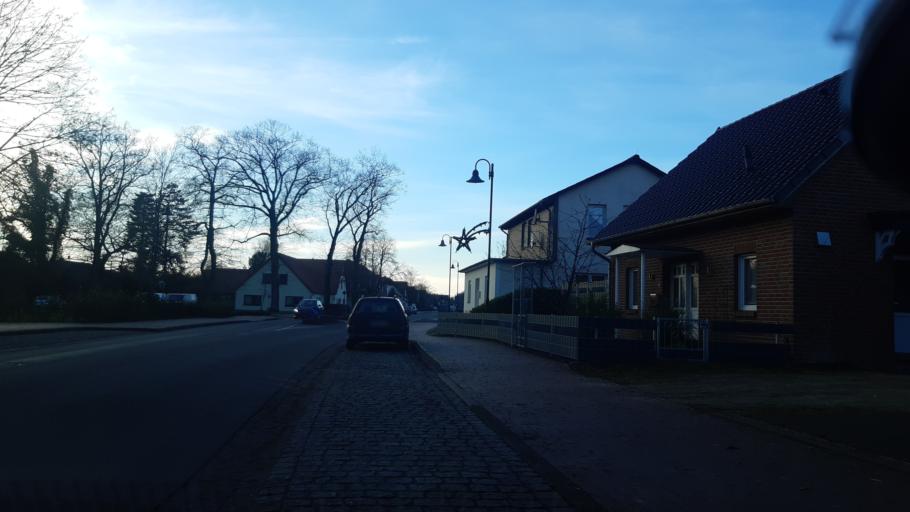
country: DE
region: Lower Saxony
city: Grossenkneten
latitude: 52.9444
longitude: 8.2546
